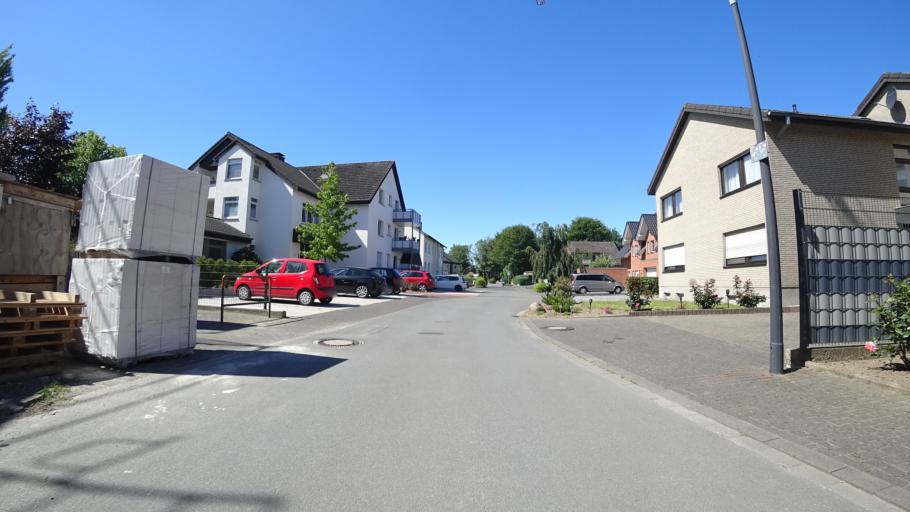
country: DE
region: North Rhine-Westphalia
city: Erwitte
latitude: 51.6281
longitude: 8.3616
